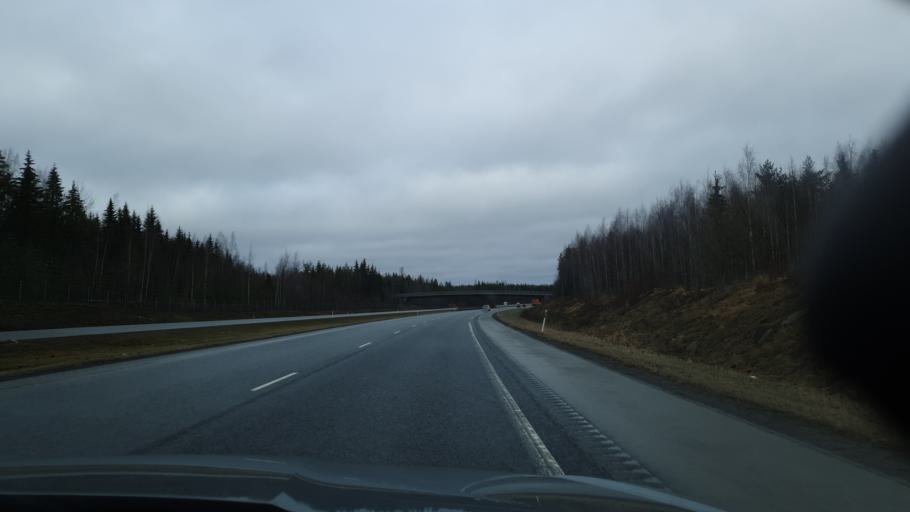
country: FI
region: Pirkanmaa
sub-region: Tampere
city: Lempaeaelae
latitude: 61.2780
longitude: 23.8110
